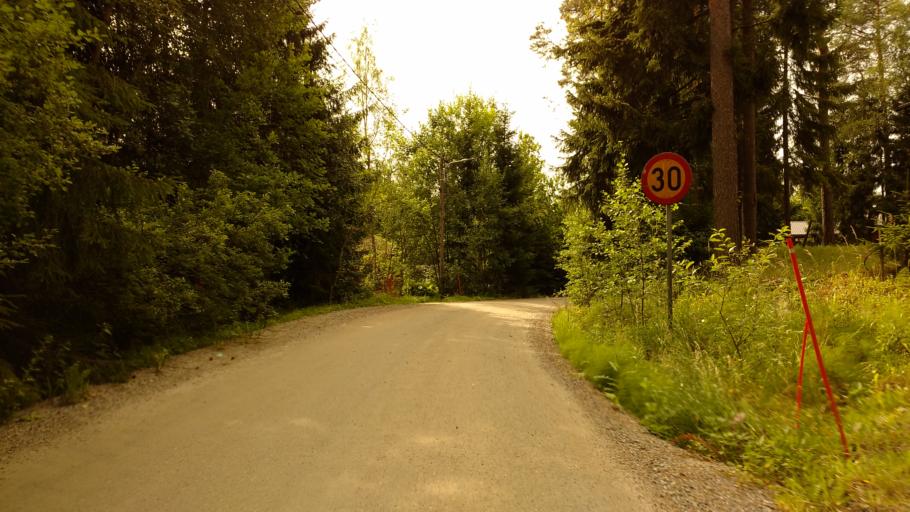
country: FI
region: Varsinais-Suomi
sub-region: Turku
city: Kaarina
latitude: 60.4457
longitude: 22.4216
